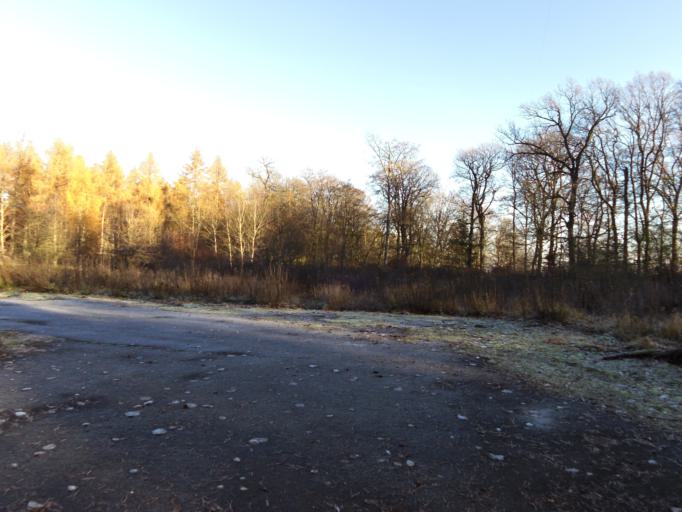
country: DE
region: Rheinland-Pfalz
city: Altleiningen
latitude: 49.4715
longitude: 8.0896
